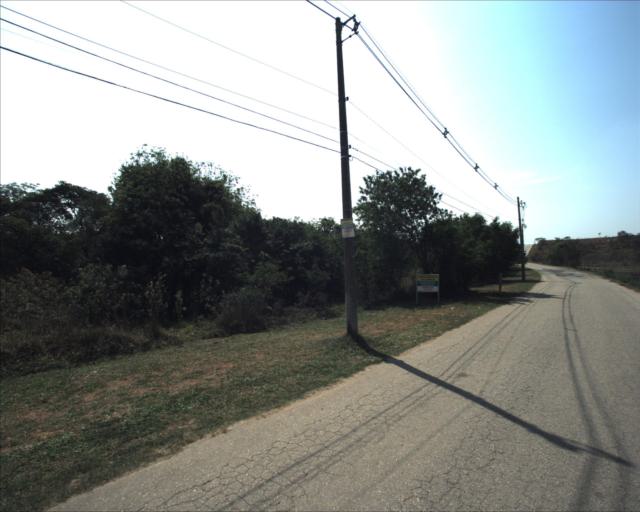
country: BR
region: Sao Paulo
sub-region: Sorocaba
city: Sorocaba
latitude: -23.4271
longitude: -47.4467
